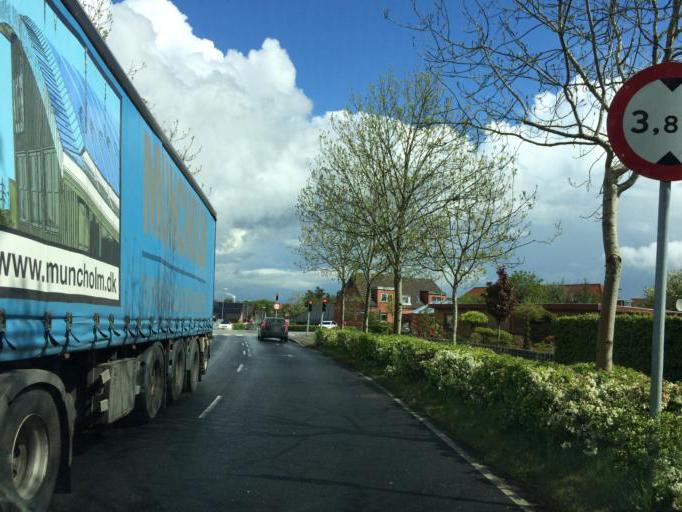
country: DK
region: Central Jutland
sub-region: Holstebro Kommune
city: Holstebro
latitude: 56.3520
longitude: 8.6058
